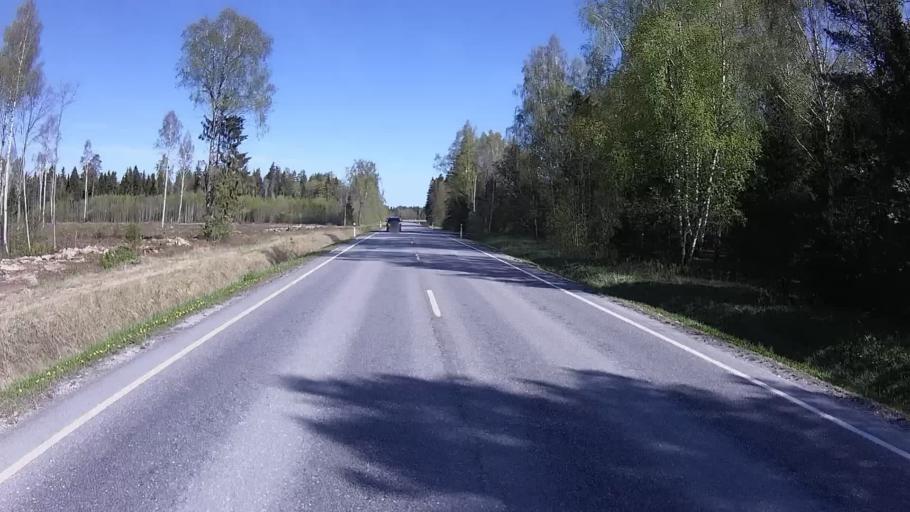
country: EE
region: Raplamaa
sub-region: Rapla vald
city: Rapla
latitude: 58.9499
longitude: 24.7624
